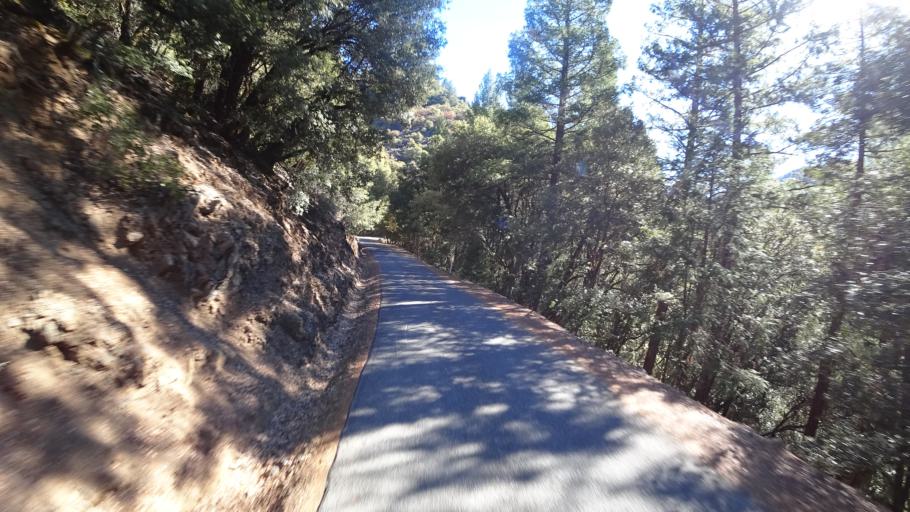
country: US
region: California
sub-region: Humboldt County
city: Willow Creek
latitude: 41.1491
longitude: -123.2062
